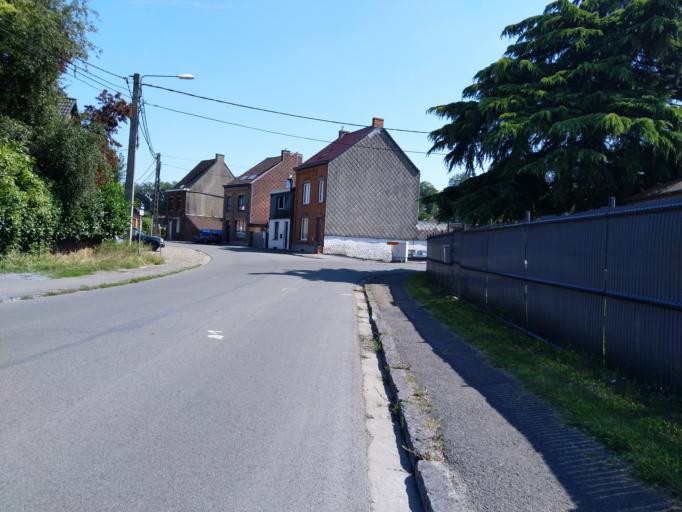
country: BE
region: Wallonia
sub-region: Province du Hainaut
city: Roeulx
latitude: 50.4746
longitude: 4.1083
